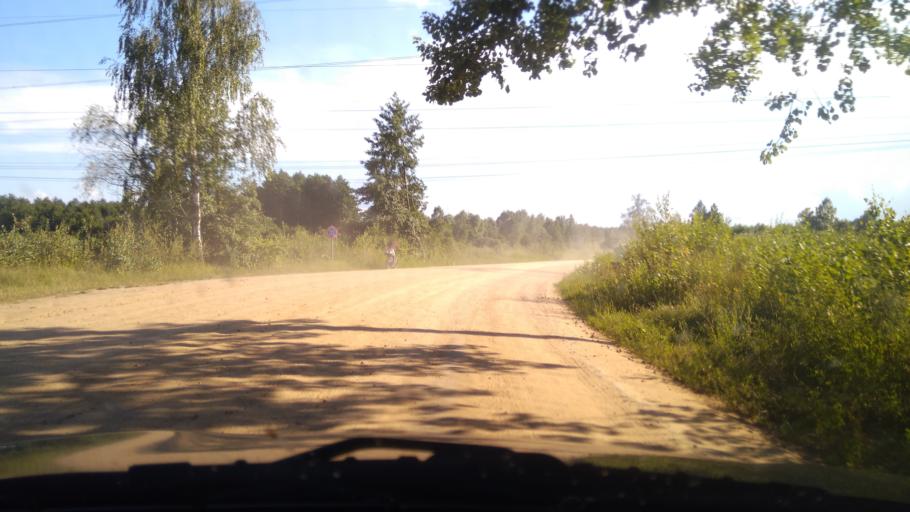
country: BY
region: Brest
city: Byelaazyorsk
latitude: 52.4502
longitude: 25.1827
